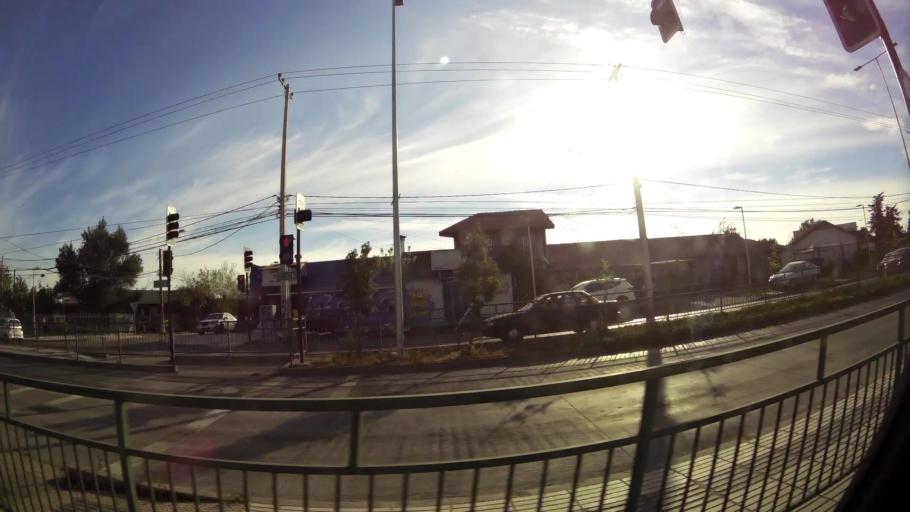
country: CL
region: Santiago Metropolitan
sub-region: Provincia de Santiago
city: Lo Prado
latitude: -33.4506
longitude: -70.7068
